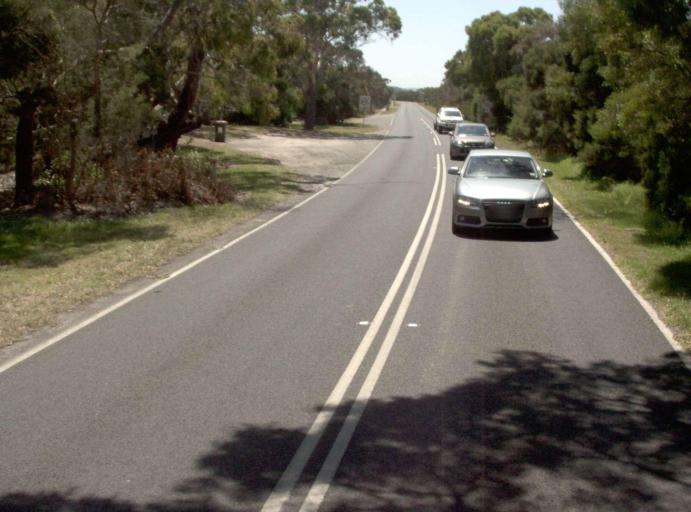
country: AU
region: Victoria
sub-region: Bass Coast
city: North Wonthaggi
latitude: -38.7020
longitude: 145.8720
